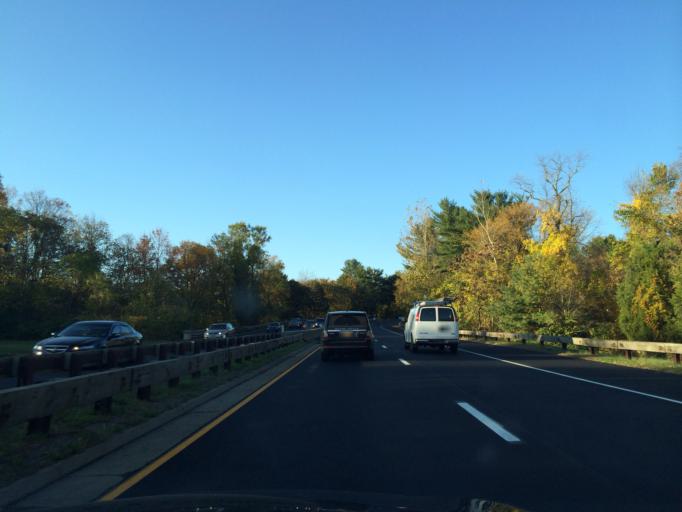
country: US
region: Connecticut
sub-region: Fairfield County
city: Glenville
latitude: 41.0579
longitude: -73.6751
